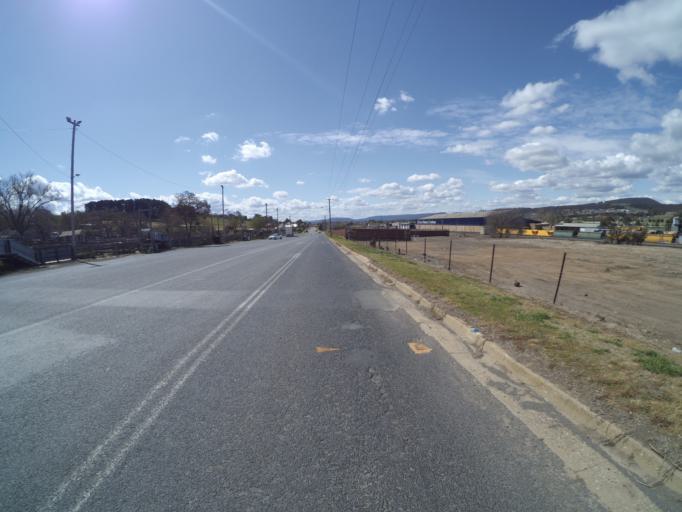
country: AU
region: New South Wales
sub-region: Goulburn Mulwaree
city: Goulburn
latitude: -34.7725
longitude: 149.7094
